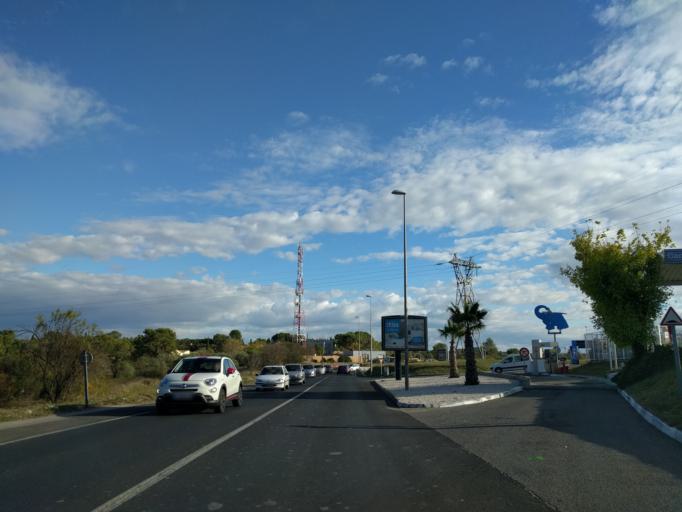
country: FR
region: Languedoc-Roussillon
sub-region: Departement de l'Herault
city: Montferrier-sur-Lez
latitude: 43.6473
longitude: 3.8434
